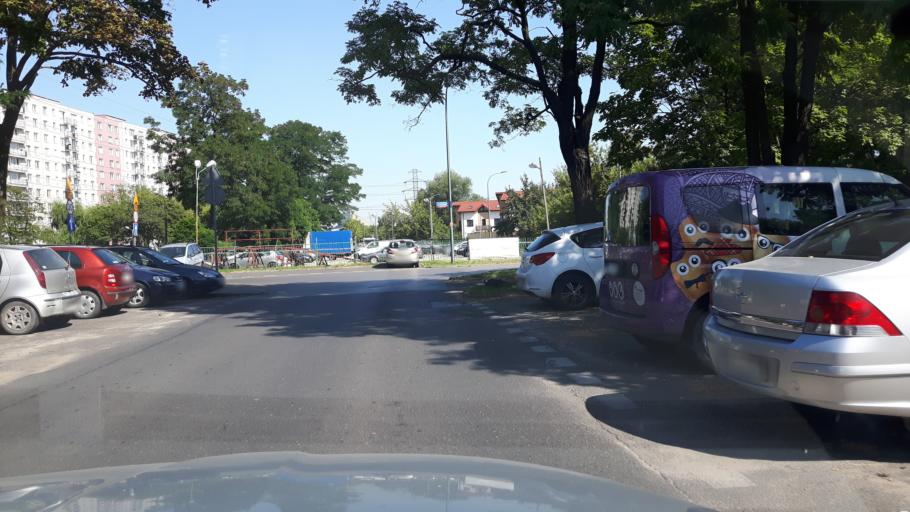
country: PL
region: Masovian Voivodeship
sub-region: Warszawa
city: Targowek
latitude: 52.2968
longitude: 21.0502
